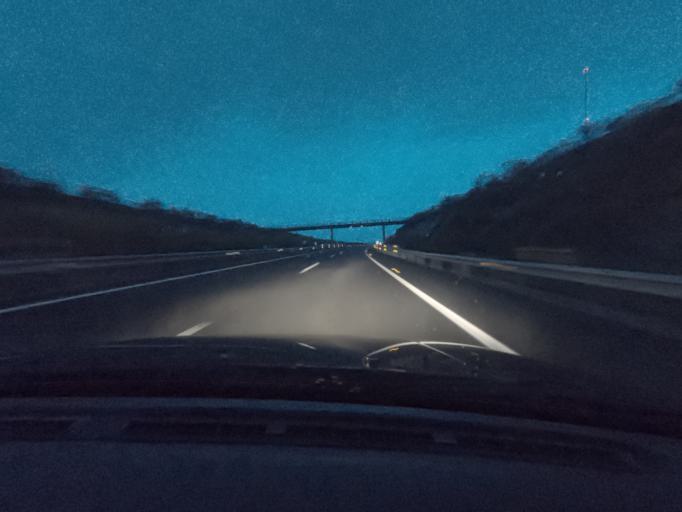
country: ES
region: Extremadura
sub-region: Provincia de Caceres
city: Aldea del Cano
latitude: 39.3445
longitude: -6.3421
